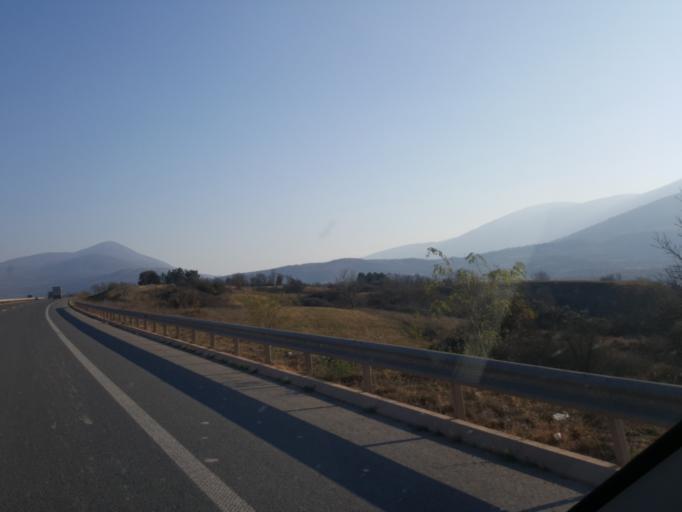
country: RS
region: Central Serbia
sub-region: Pirotski Okrug
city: Bela Palanka
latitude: 43.2459
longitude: 22.2794
